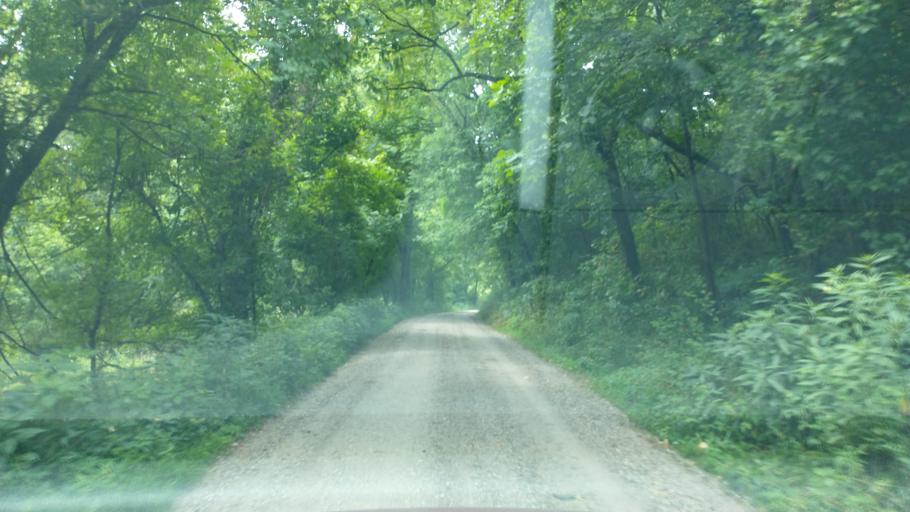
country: US
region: Ohio
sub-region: Meigs County
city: Middleport
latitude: 38.9226
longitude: -82.0492
